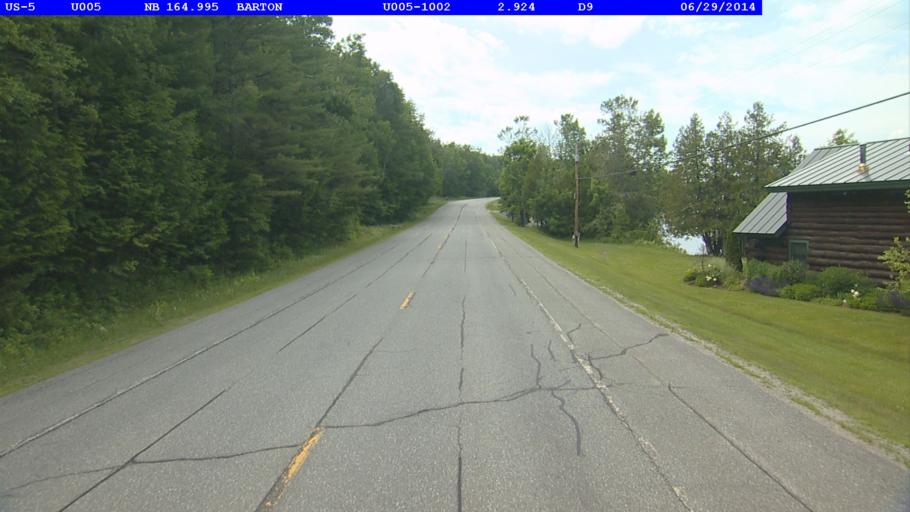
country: US
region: Vermont
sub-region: Orleans County
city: Newport
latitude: 44.7195
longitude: -72.1469
